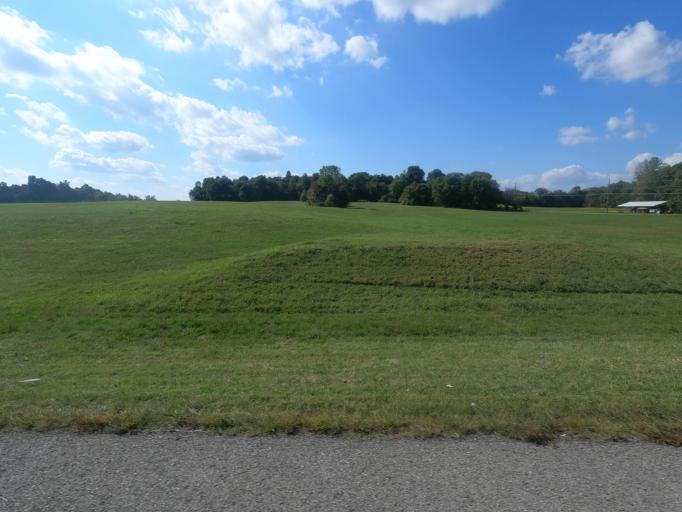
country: US
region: Illinois
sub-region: Massac County
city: Metropolis
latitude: 37.1899
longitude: -88.6766
